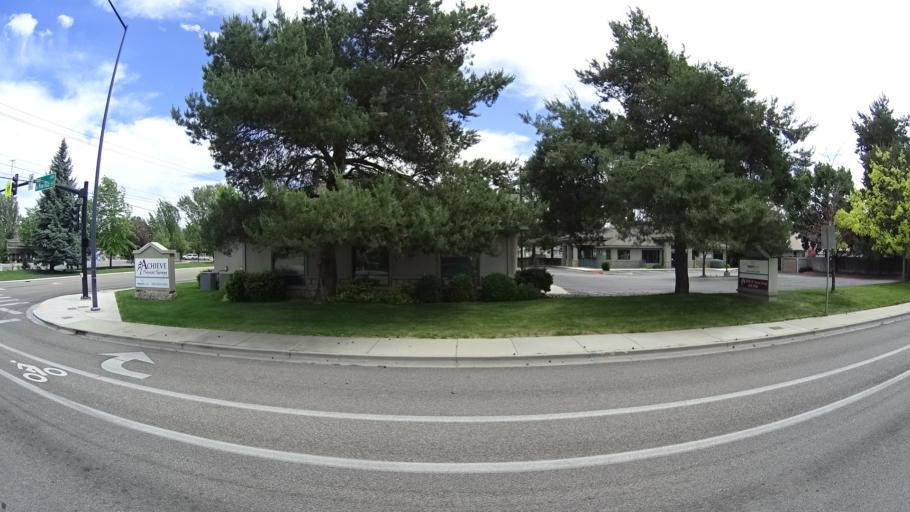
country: US
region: Idaho
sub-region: Ada County
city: Eagle
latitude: 43.6481
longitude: -116.3142
